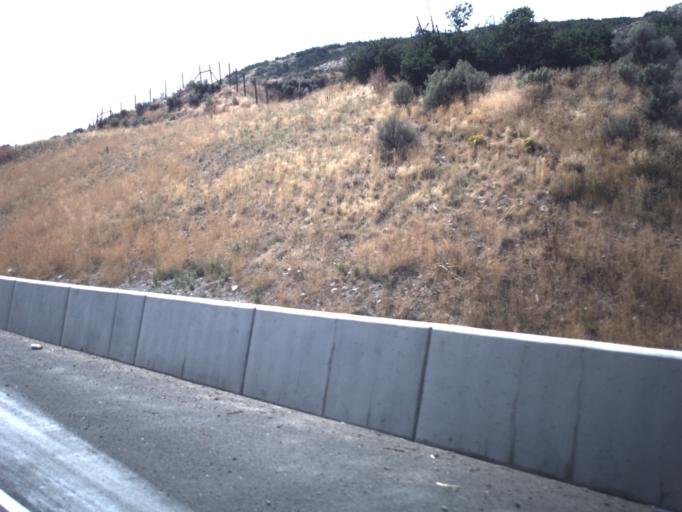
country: US
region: Utah
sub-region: Summit County
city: Coalville
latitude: 40.7931
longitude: -111.4501
